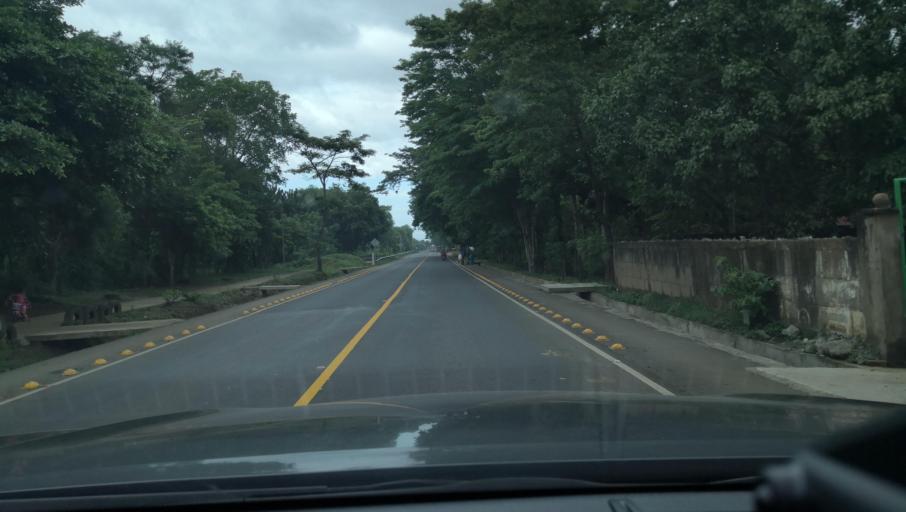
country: NI
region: Masaya
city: Nindiri
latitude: 12.0395
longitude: -86.1284
